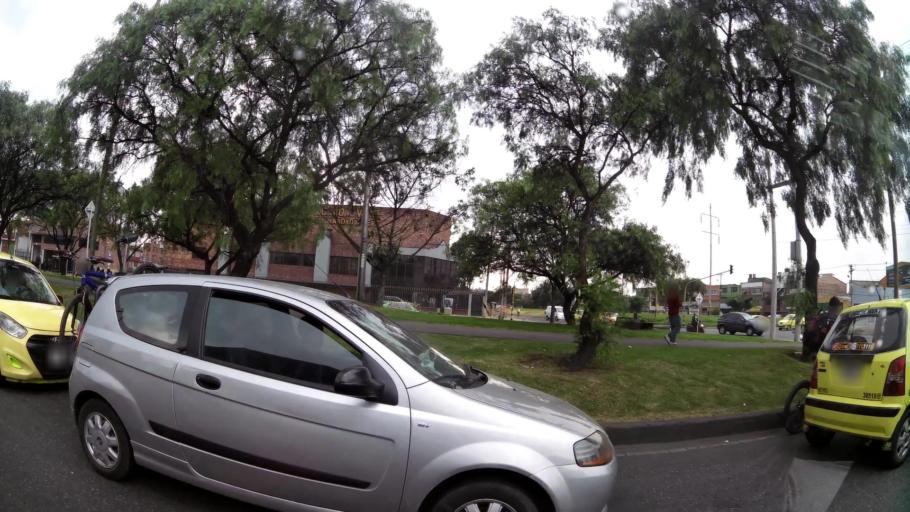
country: CO
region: Bogota D.C.
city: Bogota
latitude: 4.6182
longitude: -74.1057
